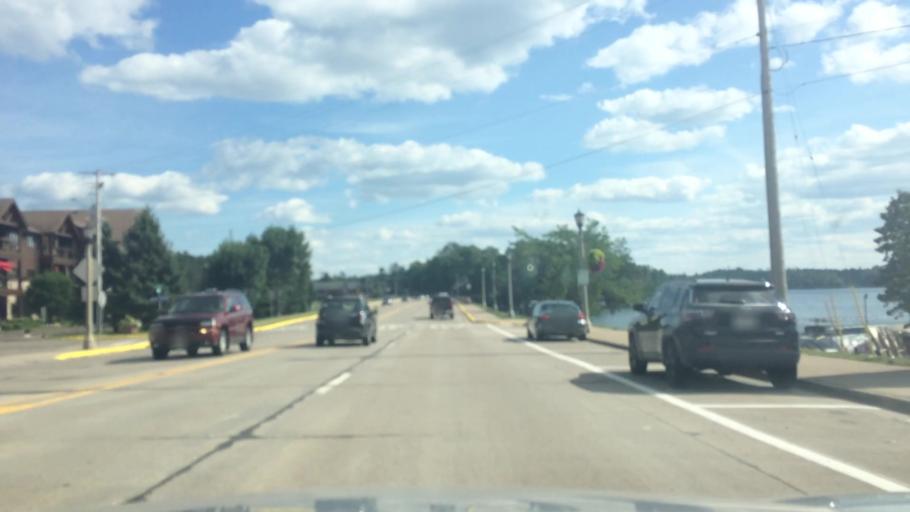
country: US
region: Wisconsin
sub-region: Vilas County
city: Lac du Flambeau
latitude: 45.8686
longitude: -89.7095
